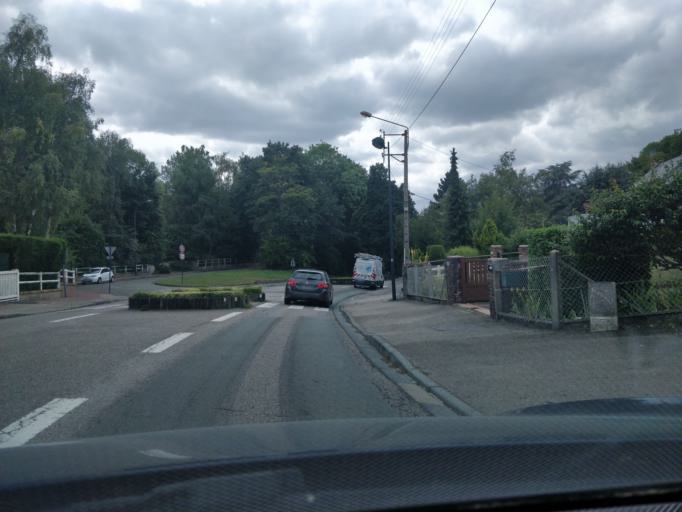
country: FR
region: Haute-Normandie
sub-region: Departement de la Seine-Maritime
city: Mont-Saint-Aignan
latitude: 49.4689
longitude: 1.1075
